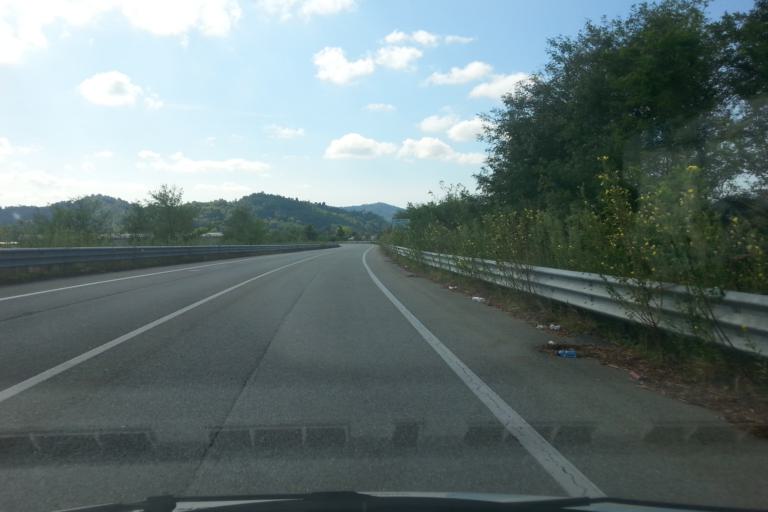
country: IT
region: Piedmont
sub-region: Provincia di Torino
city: San Raffaele Cimena
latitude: 45.1490
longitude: 7.8382
